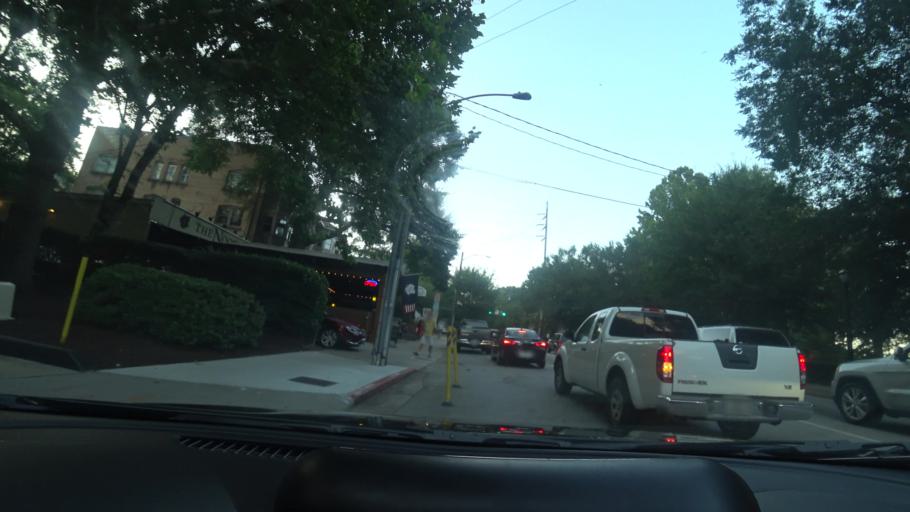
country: US
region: Georgia
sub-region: Fulton County
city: Atlanta
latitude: 33.7858
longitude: -84.3780
